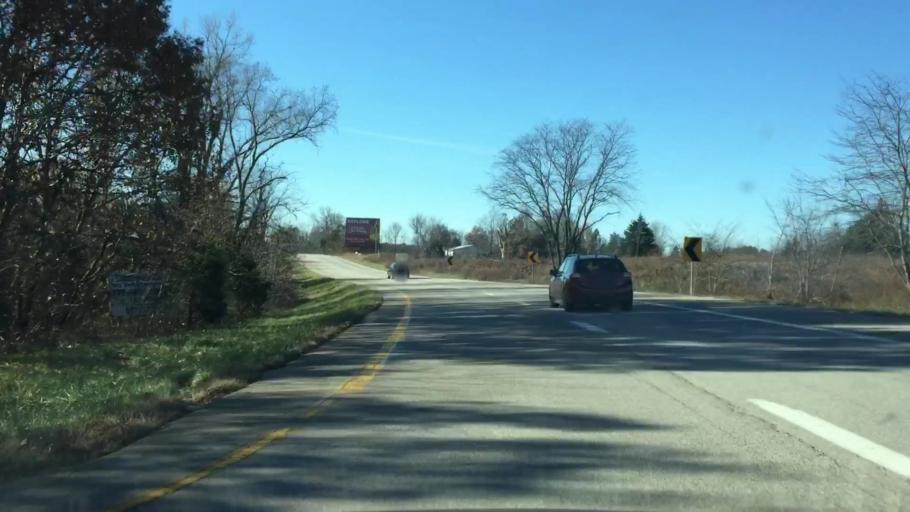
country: US
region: Missouri
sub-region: Cole County
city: Wardsville
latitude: 38.4311
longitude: -92.3222
